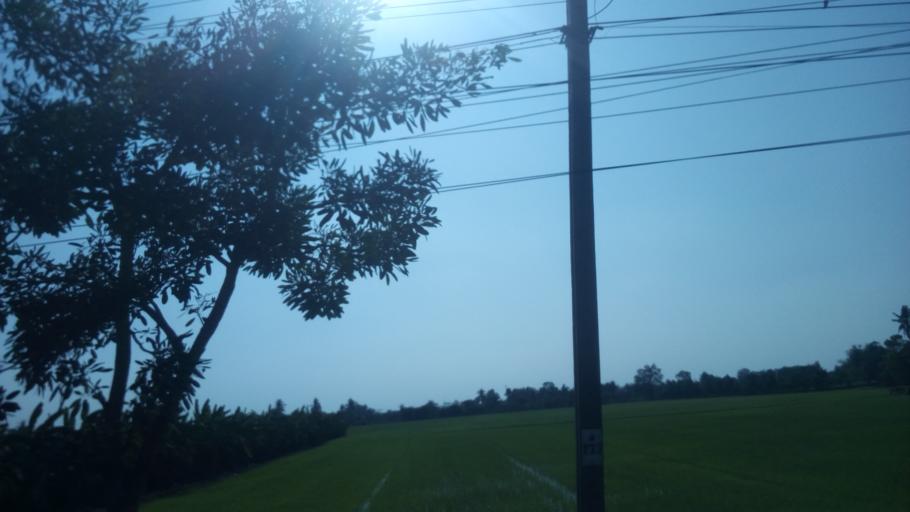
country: TH
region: Nonthaburi
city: Bang Yai
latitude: 13.8950
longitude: 100.3256
